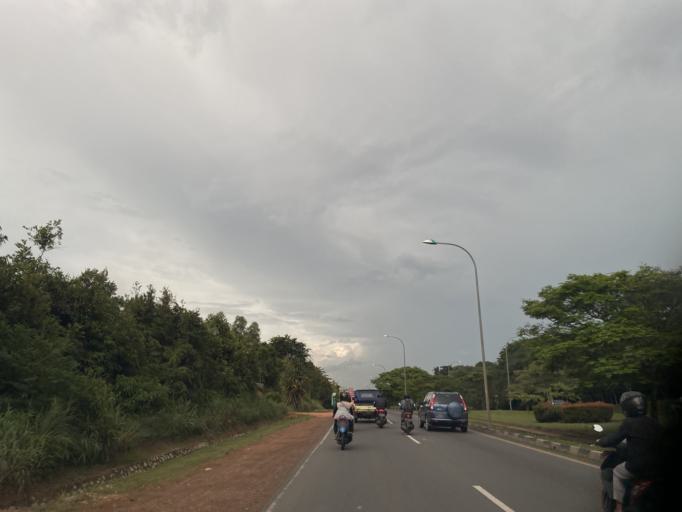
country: SG
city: Singapore
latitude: 1.0999
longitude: 104.0721
